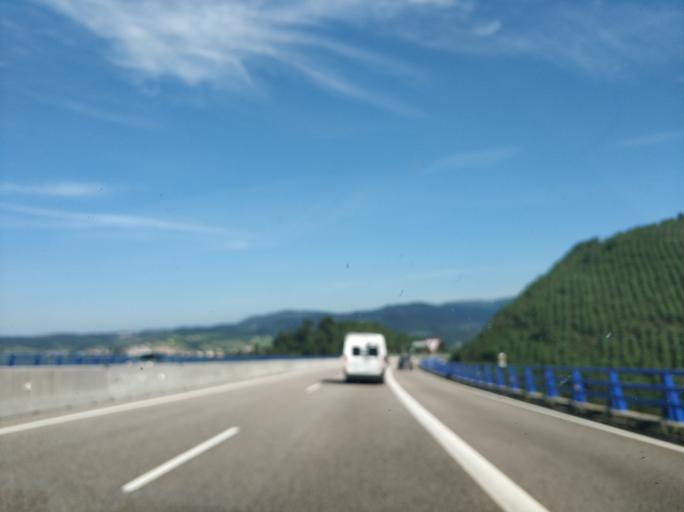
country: ES
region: Asturias
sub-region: Province of Asturias
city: Muros de Nalon
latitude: 43.5356
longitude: -6.1055
